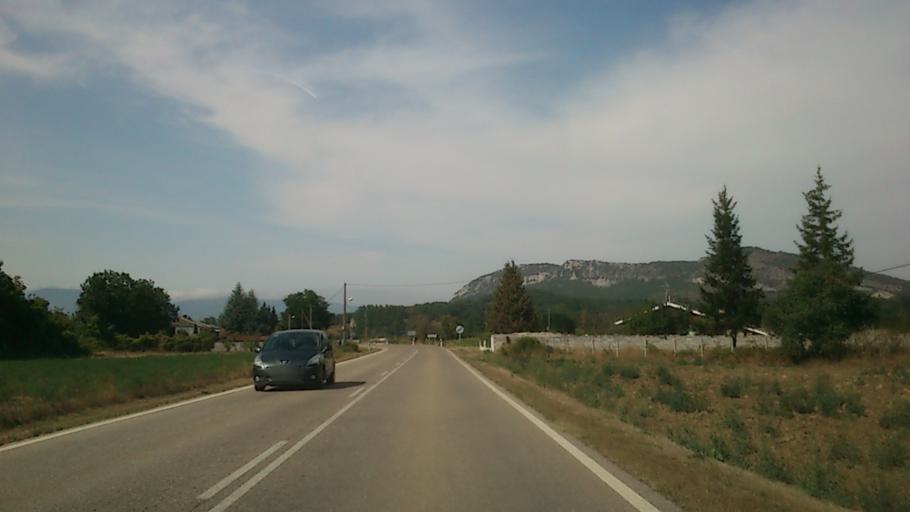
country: ES
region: Castille and Leon
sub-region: Provincia de Burgos
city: Medina de Pomar
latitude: 43.0082
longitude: -3.4823
